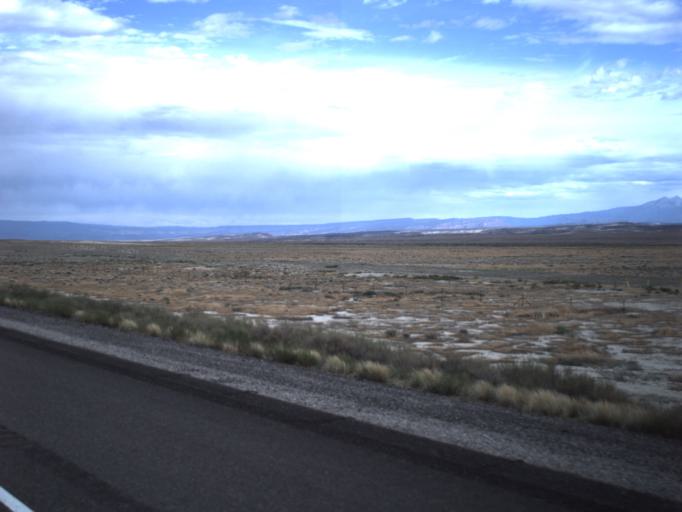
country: US
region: Utah
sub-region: Grand County
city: Moab
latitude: 38.9418
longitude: -109.5539
